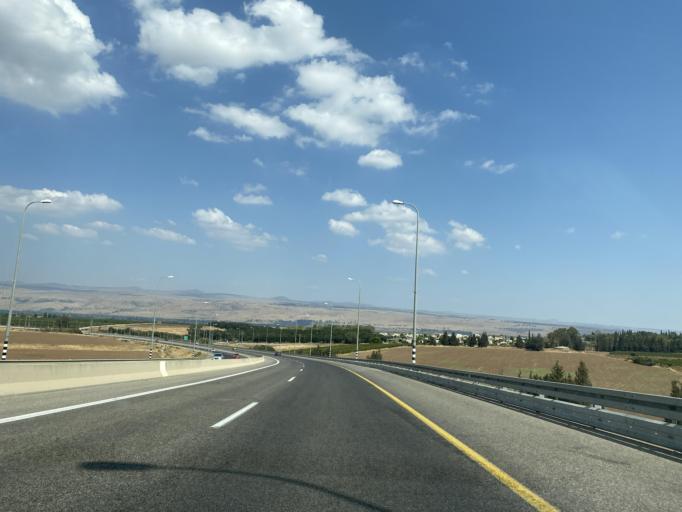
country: IL
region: Northern District
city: Rosh Pinna
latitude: 33.0282
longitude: 35.5651
